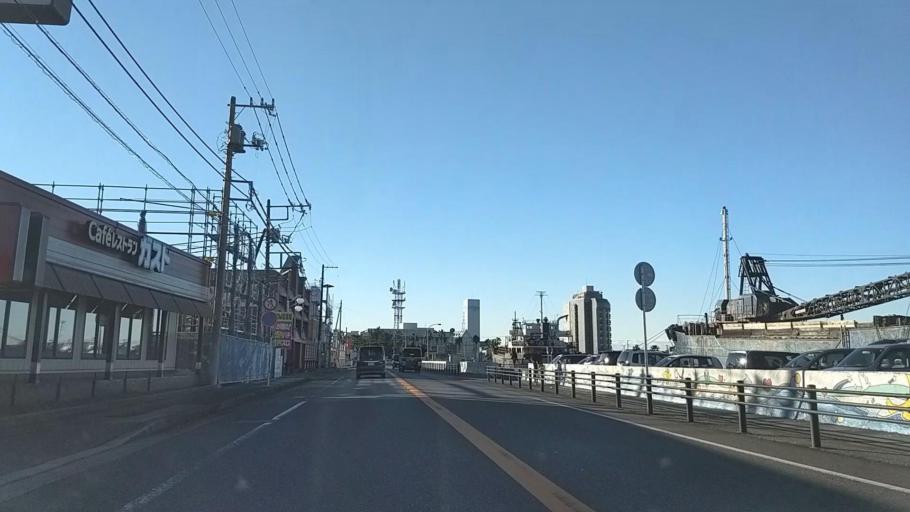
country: JP
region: Chiba
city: Kisarazu
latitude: 35.3842
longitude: 139.9181
